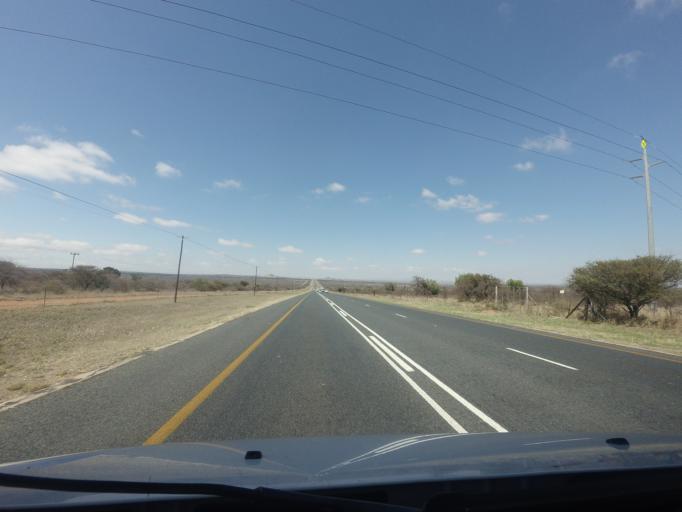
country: ZA
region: Limpopo
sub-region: Vhembe District Municipality
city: Louis Trichardt
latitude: -23.3797
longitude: 29.7673
